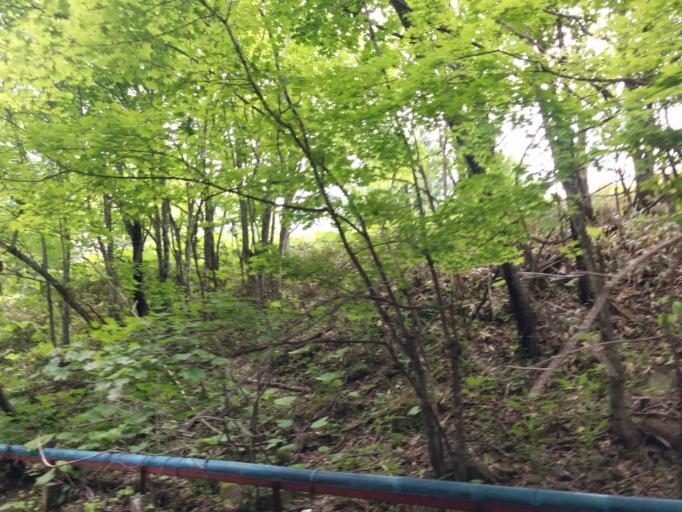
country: JP
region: Hokkaido
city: Otofuke
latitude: 43.3665
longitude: 143.1937
